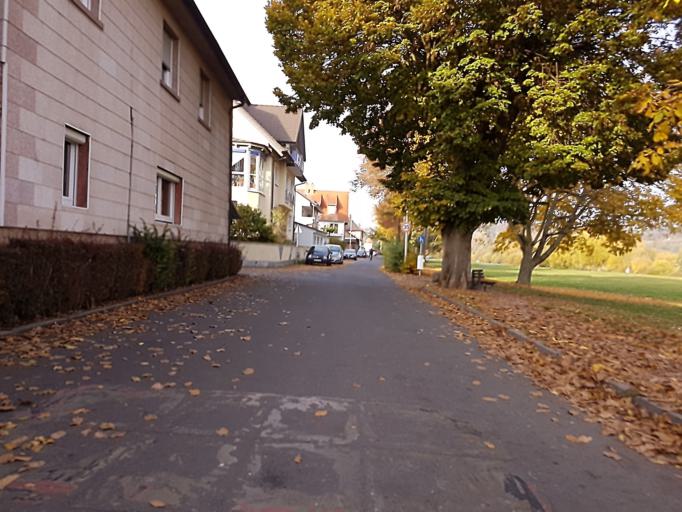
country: DE
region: Bavaria
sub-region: Regierungsbezirk Unterfranken
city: Kleinwallstadt
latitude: 49.8767
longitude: 9.1604
